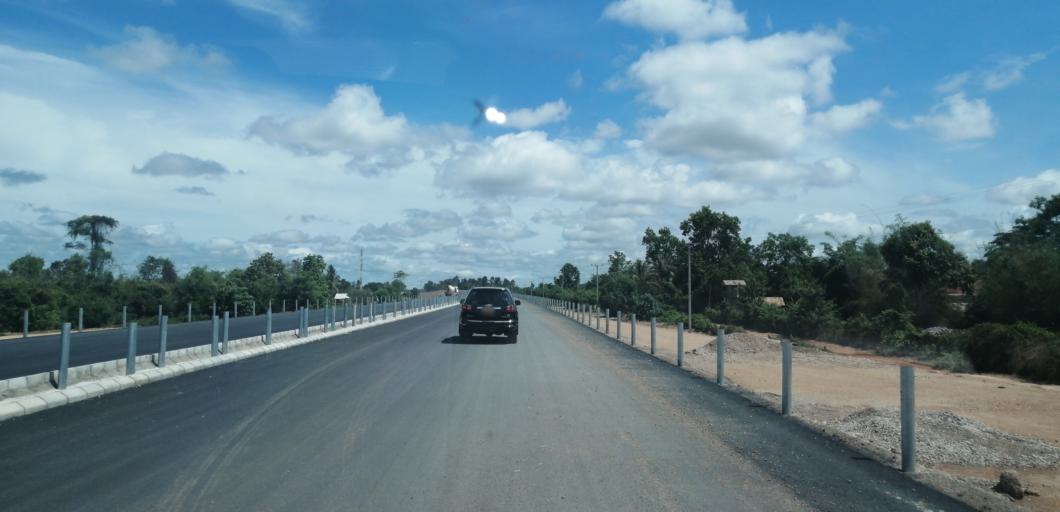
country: LA
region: Vientiane
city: Vientiane
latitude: 18.0531
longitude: 102.5243
